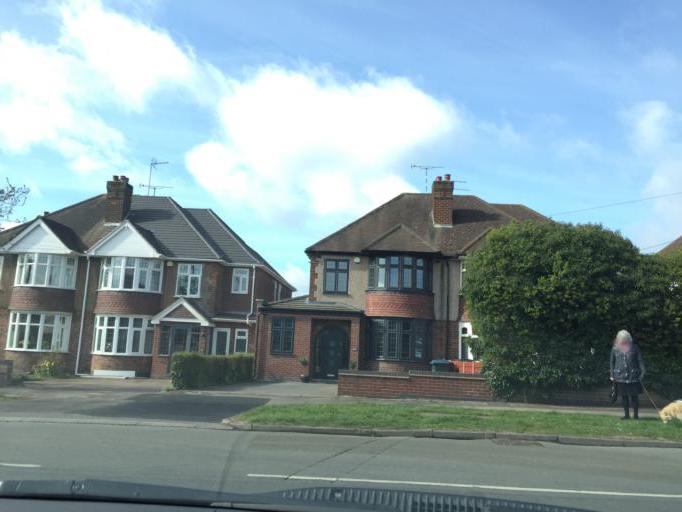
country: GB
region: England
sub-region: Coventry
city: Coventry
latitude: 52.3840
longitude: -1.5129
